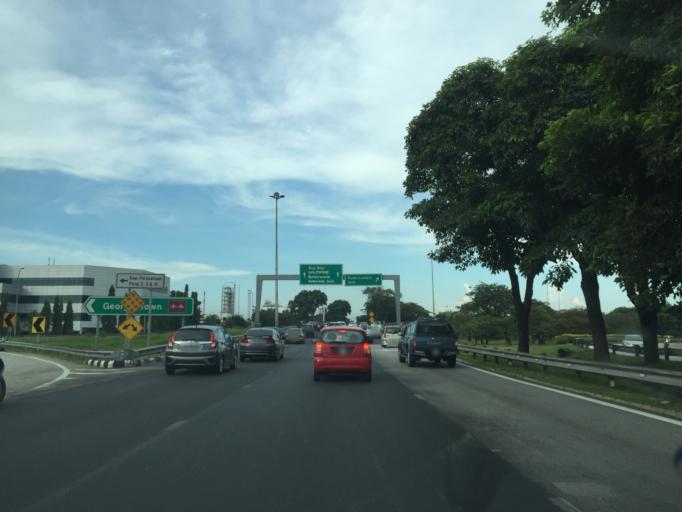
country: MY
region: Penang
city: Perai
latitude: 5.3653
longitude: 100.3970
